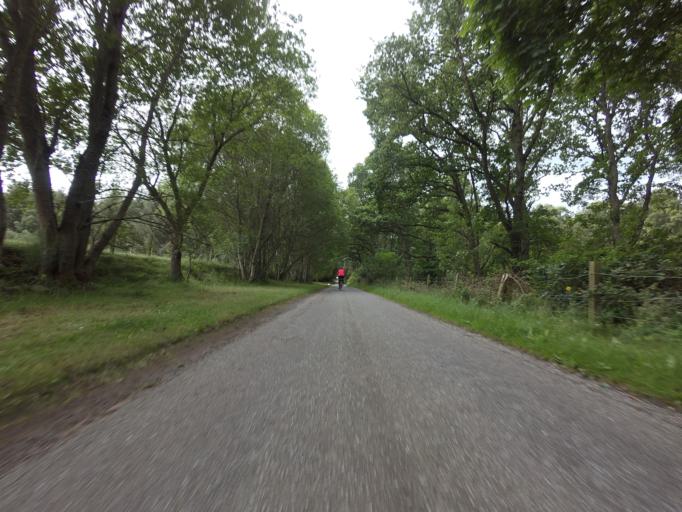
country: GB
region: Scotland
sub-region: Highland
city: Nairn
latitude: 57.6009
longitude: -3.7843
